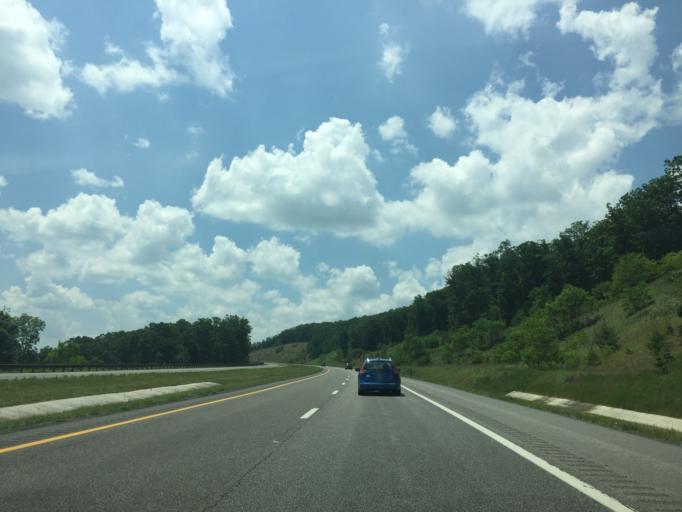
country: US
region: Virginia
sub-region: Shenandoah County
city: Woodstock
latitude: 39.0655
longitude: -78.6733
